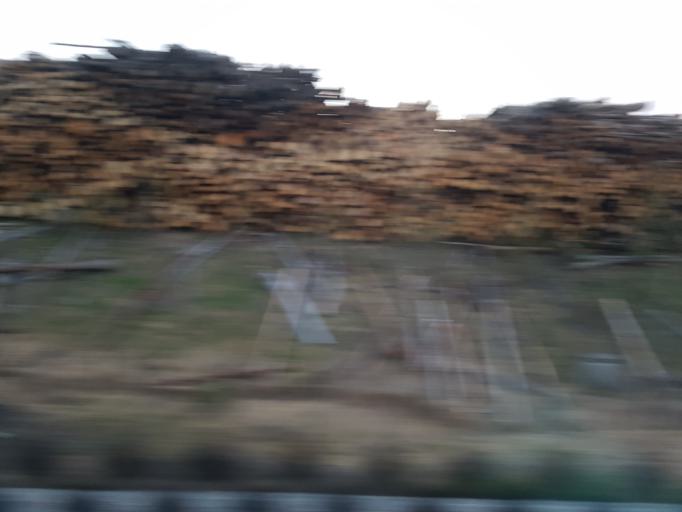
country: NO
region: Hedmark
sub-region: Ringsaker
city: Moelv
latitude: 60.9154
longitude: 10.8087
